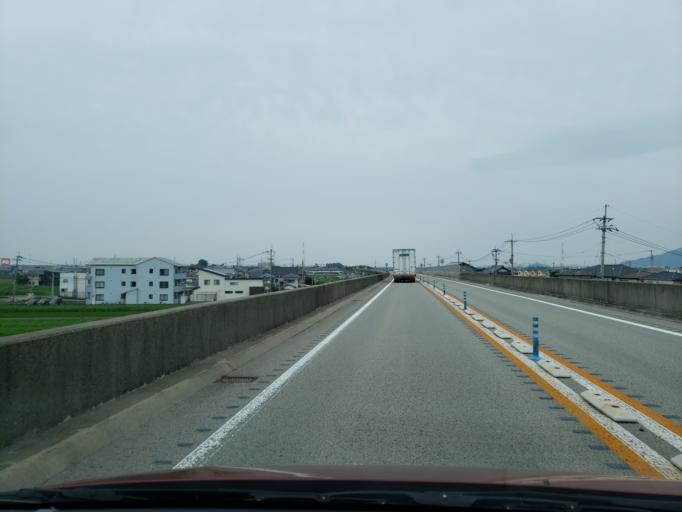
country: JP
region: Tokushima
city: Ishii
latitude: 34.1145
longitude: 134.4934
